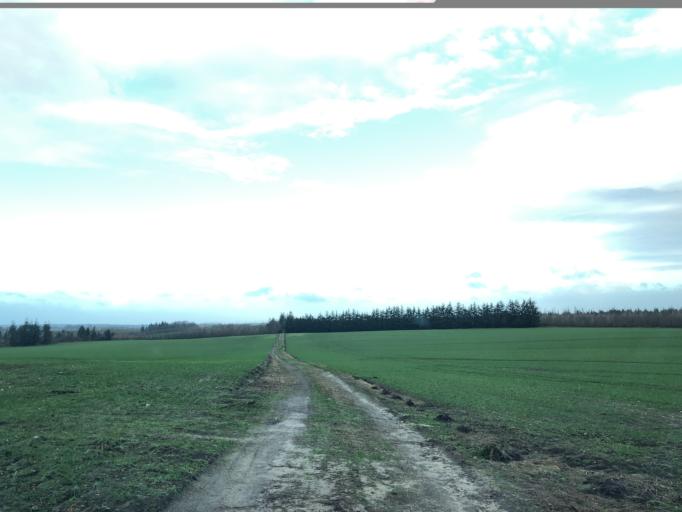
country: DK
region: Central Jutland
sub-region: Ringkobing-Skjern Kommune
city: Videbaek
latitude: 56.1869
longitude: 8.6600
